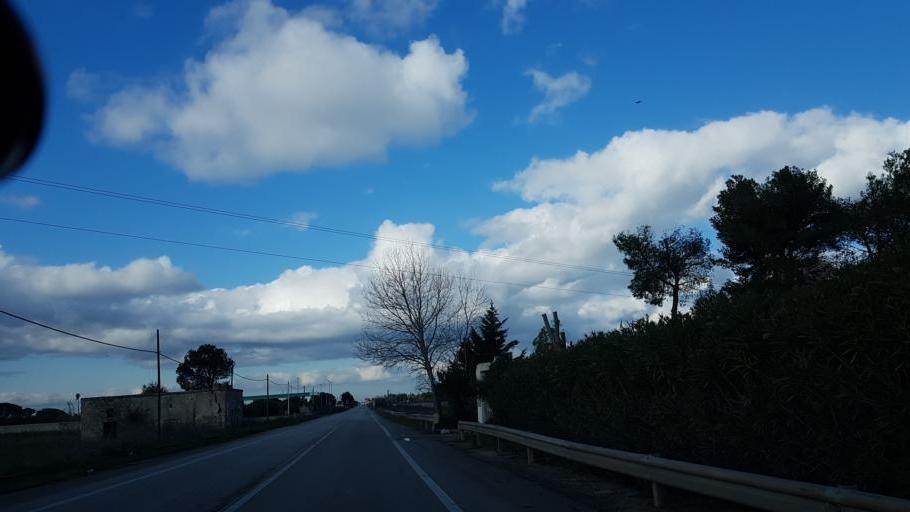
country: IT
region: Apulia
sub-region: Provincia di Brindisi
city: Brindisi
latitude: 40.6463
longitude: 17.8956
